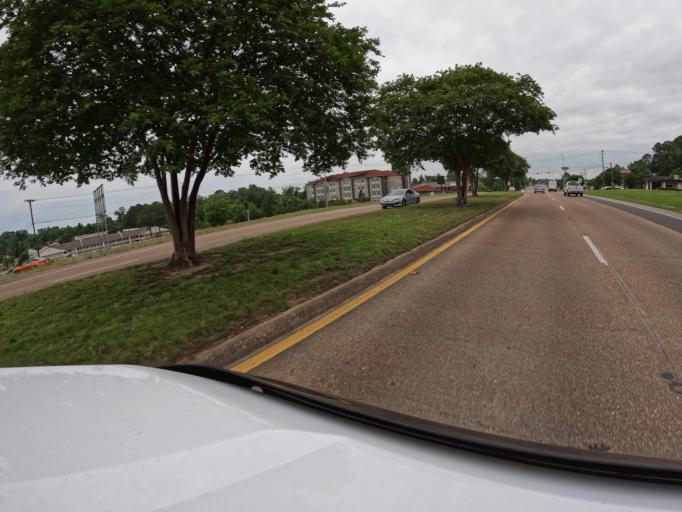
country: US
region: Mississippi
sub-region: Lee County
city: Tupelo
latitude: 34.2757
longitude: -88.7155
